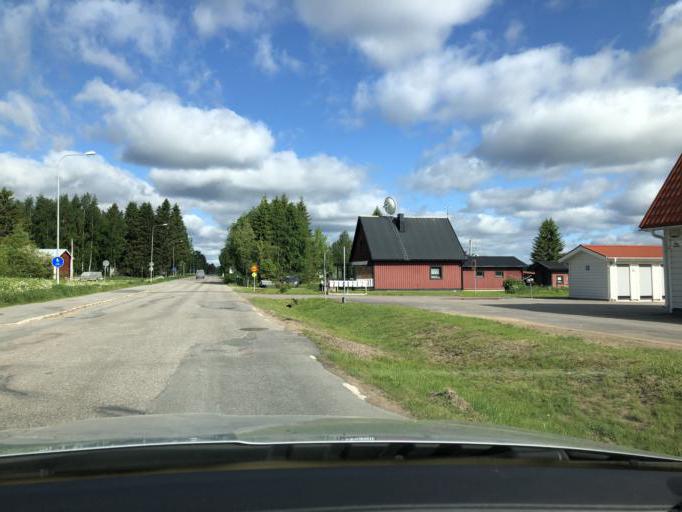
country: SE
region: Norrbotten
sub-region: Pajala Kommun
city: Pajala
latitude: 67.2186
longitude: 23.3548
